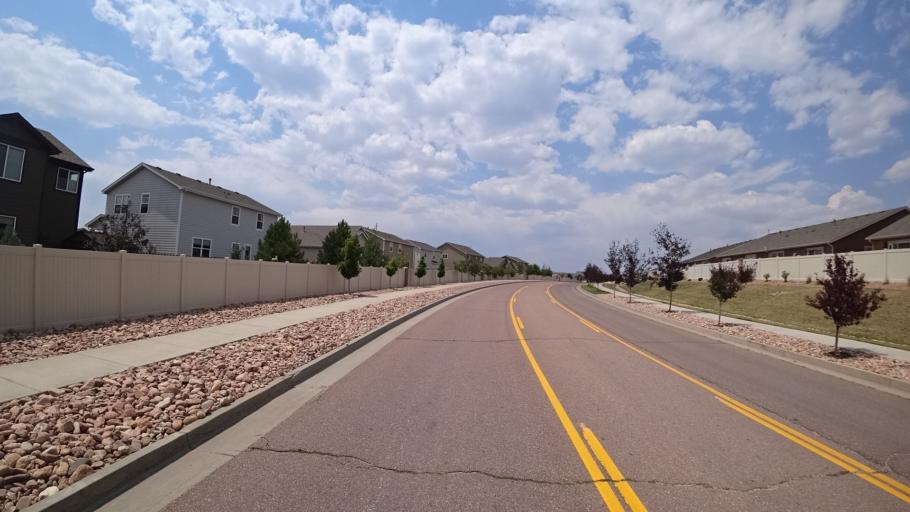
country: US
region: Colorado
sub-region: El Paso County
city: Black Forest
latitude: 38.9481
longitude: -104.6925
